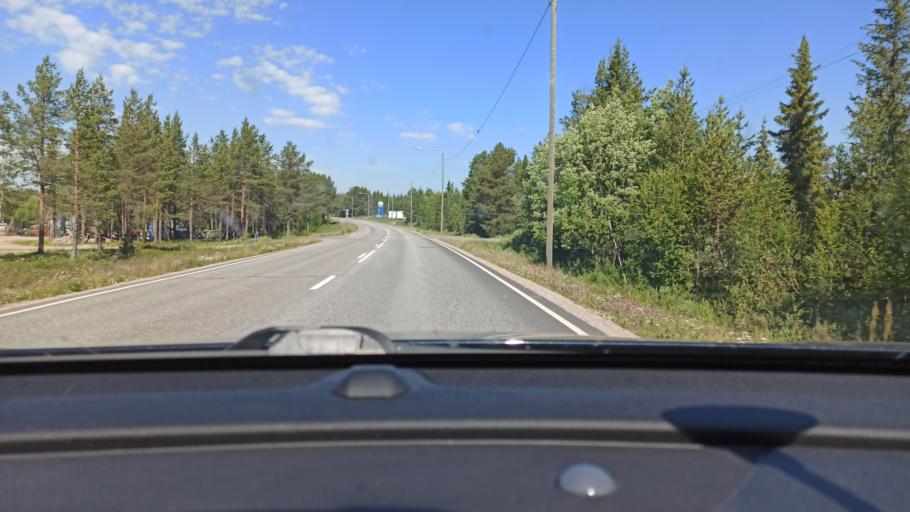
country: FI
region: Lapland
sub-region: Tunturi-Lappi
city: Muonio
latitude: 67.9705
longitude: 23.6807
